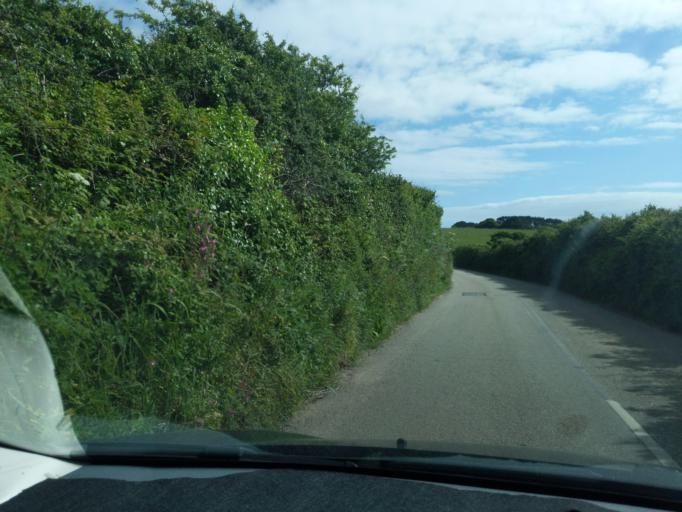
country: GB
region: England
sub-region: Cornwall
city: St. Buryan
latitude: 50.0662
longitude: -5.6339
